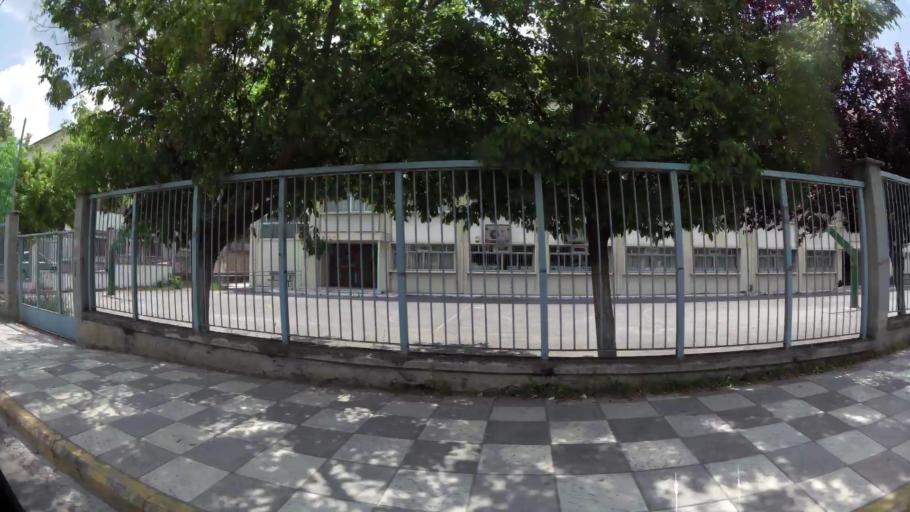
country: GR
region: West Macedonia
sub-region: Nomos Kozanis
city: Kozani
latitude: 40.2927
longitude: 21.7899
